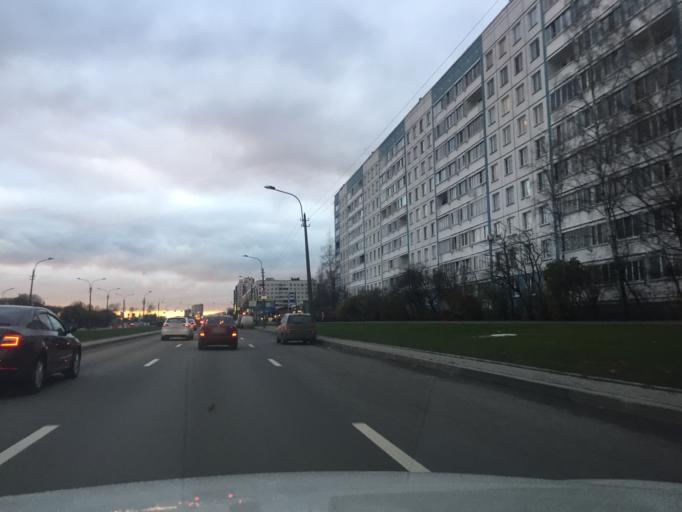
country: RU
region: St.-Petersburg
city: Grazhdanka
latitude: 60.0247
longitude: 30.4145
